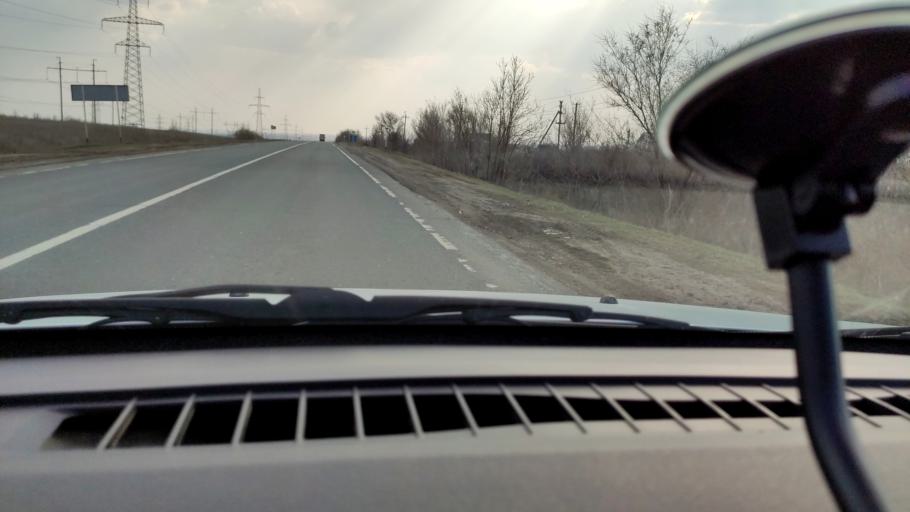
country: RU
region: Samara
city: Dubovyy Umet
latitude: 53.0724
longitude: 50.3830
